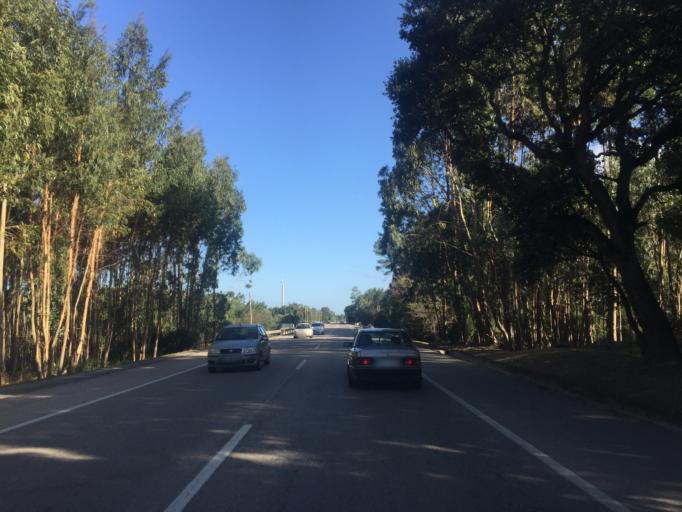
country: PT
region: Leiria
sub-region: Alcobaca
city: Turquel
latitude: 39.4967
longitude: -8.9300
